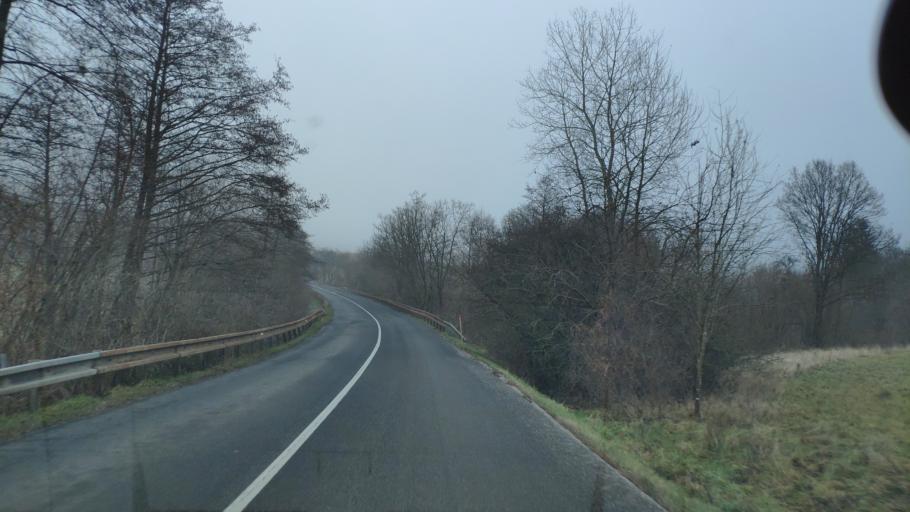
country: SK
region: Kosicky
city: Dobsina
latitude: 48.6358
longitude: 20.3340
